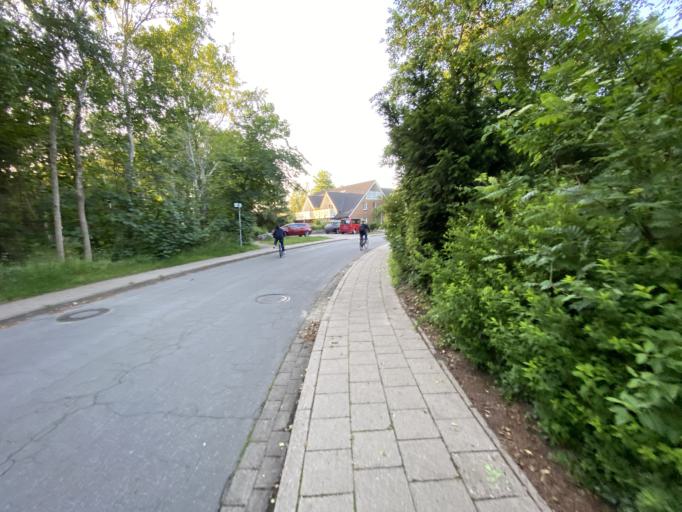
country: DE
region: Schleswig-Holstein
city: Sankt Peter-Ording
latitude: 54.3126
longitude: 8.6192
